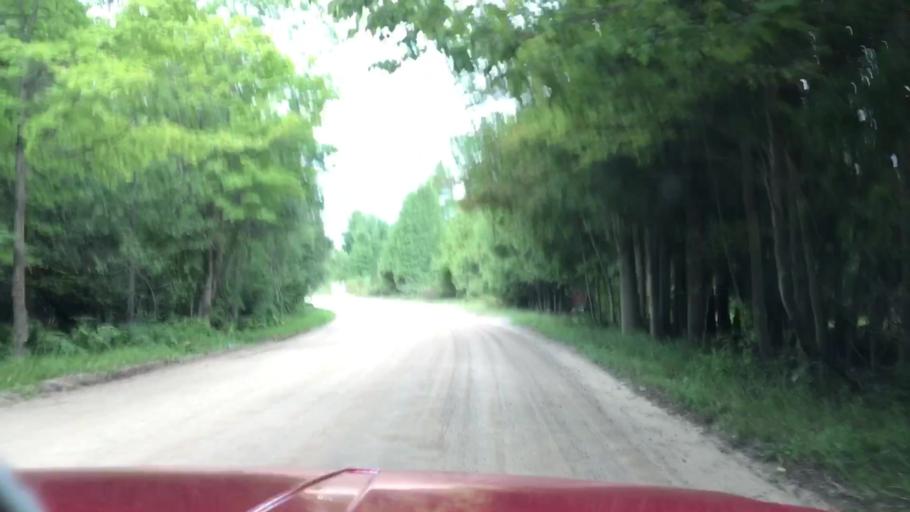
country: US
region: Michigan
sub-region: Charlevoix County
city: Charlevoix
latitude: 45.7289
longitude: -85.5409
